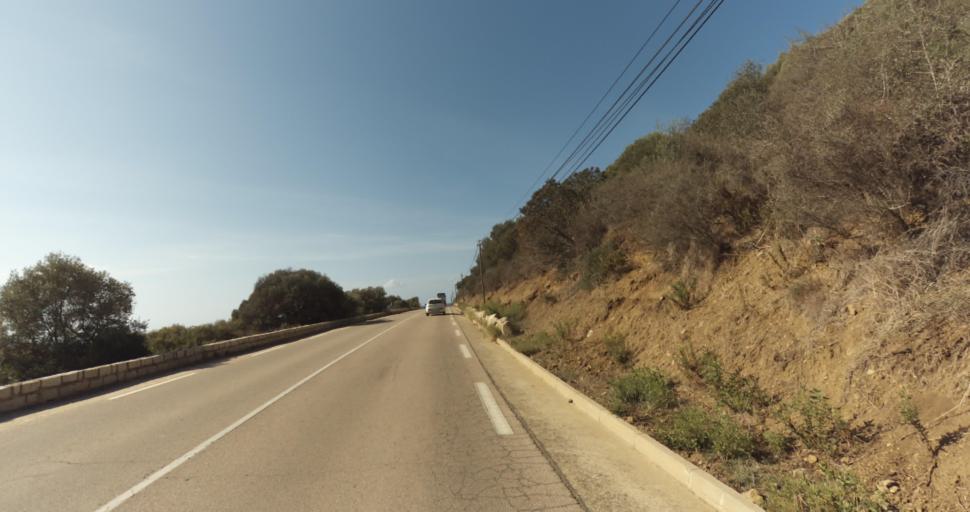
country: FR
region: Corsica
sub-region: Departement de la Corse-du-Sud
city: Ajaccio
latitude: 41.9049
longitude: 8.6267
